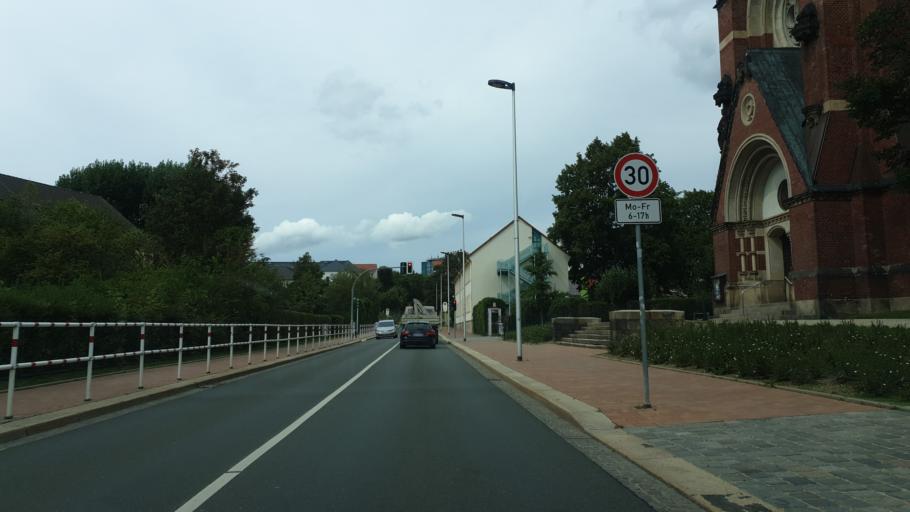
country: DE
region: Saxony
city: Plauen
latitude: 50.5020
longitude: 12.1396
